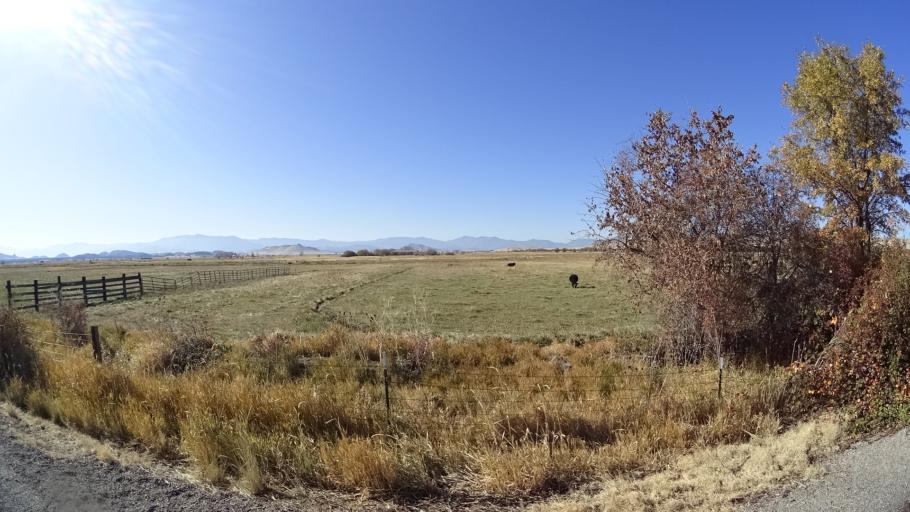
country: US
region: California
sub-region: Siskiyou County
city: Montague
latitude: 41.7211
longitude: -122.3892
